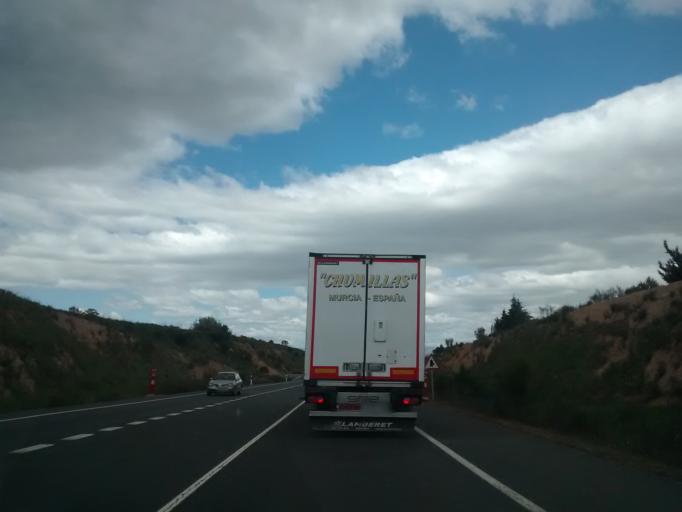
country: ES
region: La Rioja
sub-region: Provincia de La Rioja
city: Ausejo
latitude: 42.3462
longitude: -2.1792
